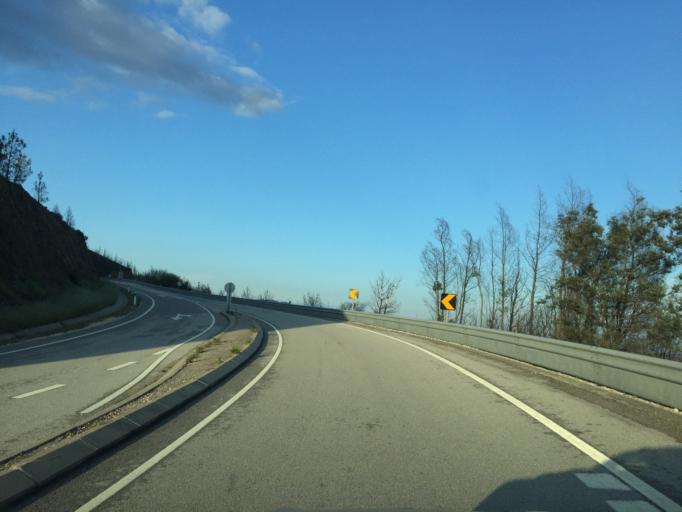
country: PT
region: Coimbra
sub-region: Gois
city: Gois
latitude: 40.0799
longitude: -8.0726
